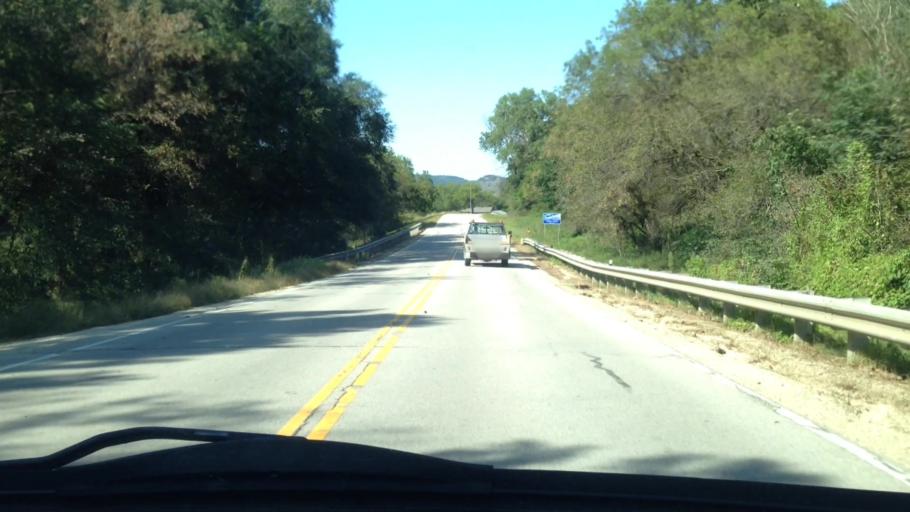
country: US
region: Minnesota
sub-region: Fillmore County
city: Rushford
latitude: 43.7677
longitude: -91.7634
